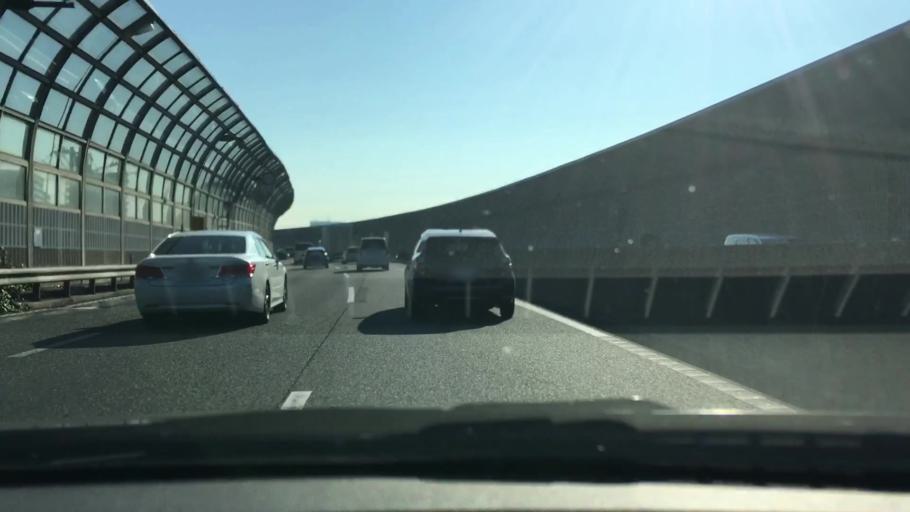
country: JP
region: Chiba
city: Funabashi
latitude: 35.6949
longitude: 139.9759
